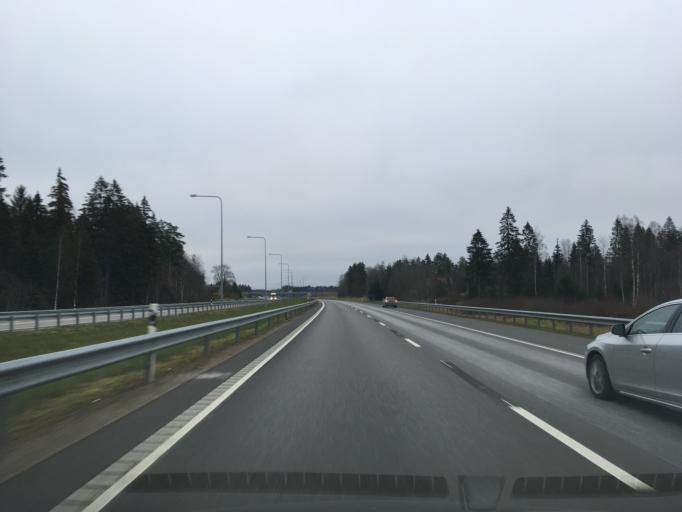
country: EE
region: Laeaene-Virumaa
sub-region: Tapa vald
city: Tapa
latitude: 59.4540
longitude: 25.9300
